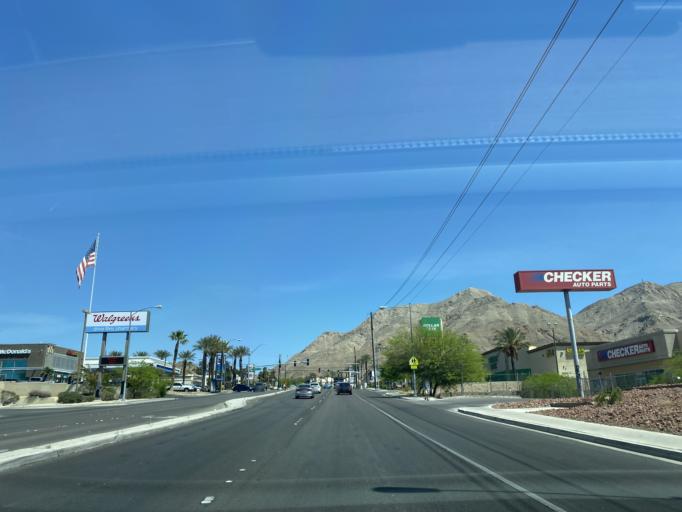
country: US
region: Nevada
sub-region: Clark County
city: Sunrise Manor
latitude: 36.1956
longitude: -115.0283
